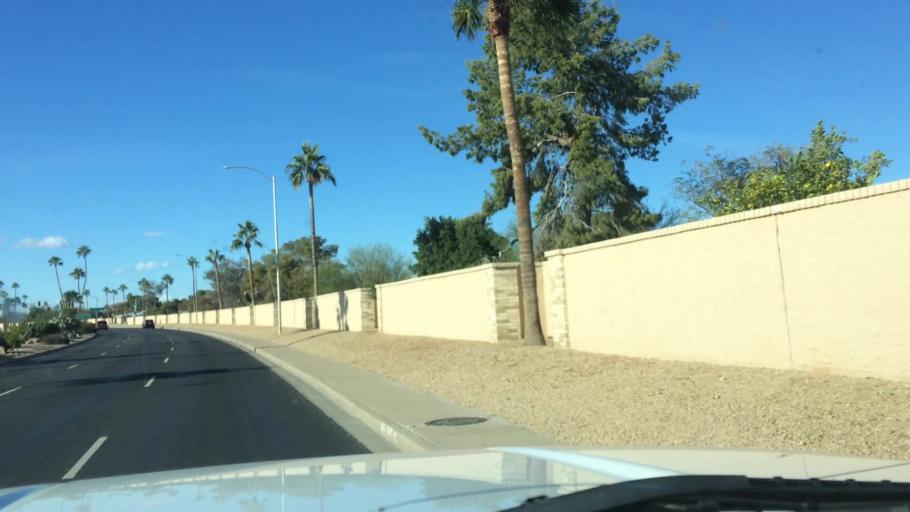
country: US
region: Arizona
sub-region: Maricopa County
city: Sun City West
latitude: 33.6479
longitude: -112.3357
